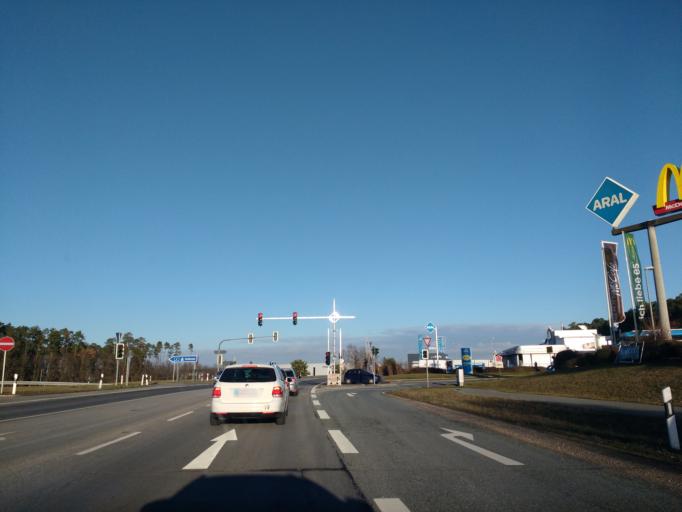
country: DE
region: Bavaria
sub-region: Regierungsbezirk Mittelfranken
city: Schwabach
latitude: 49.3110
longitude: 11.0006
